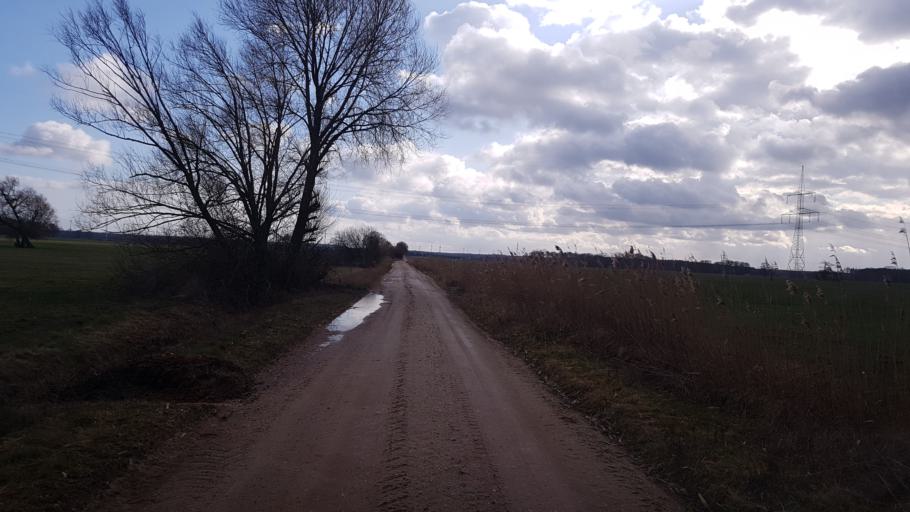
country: DE
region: Brandenburg
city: Sallgast
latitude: 51.6315
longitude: 13.8566
